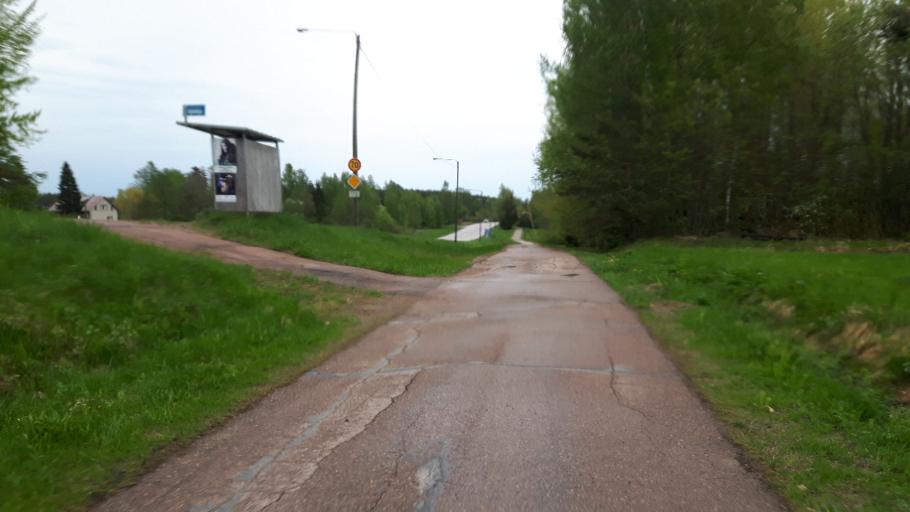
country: FI
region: Kymenlaakso
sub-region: Kotka-Hamina
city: Karhula
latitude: 60.5613
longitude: 27.0380
